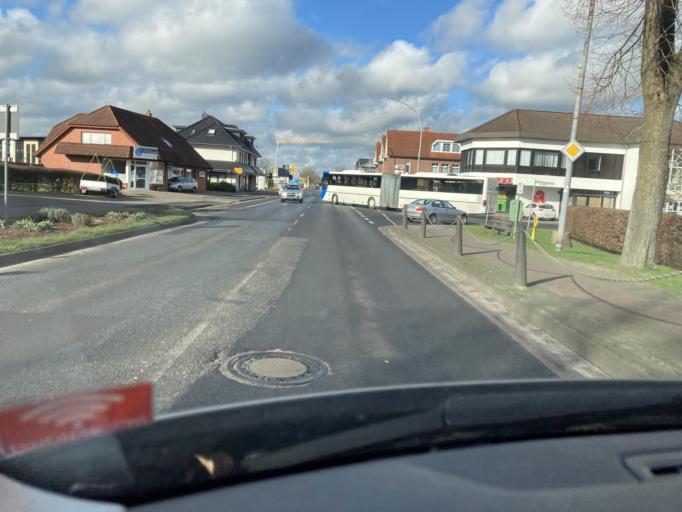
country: DE
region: Lower Saxony
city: Ostrhauderfehn
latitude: 53.1362
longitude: 7.5747
